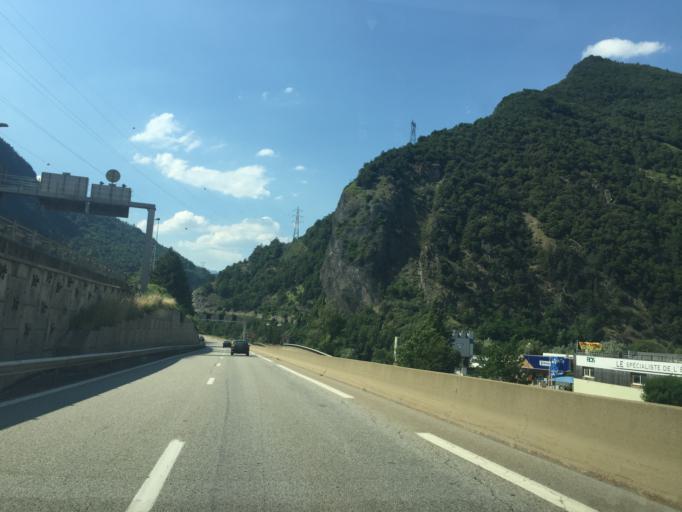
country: FR
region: Rhone-Alpes
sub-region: Departement de la Savoie
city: Moutiers
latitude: 45.4845
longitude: 6.5243
